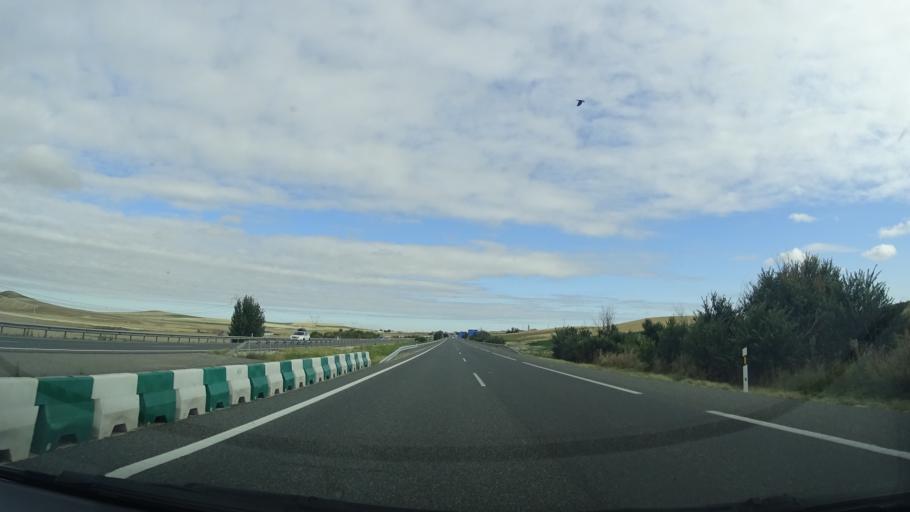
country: ES
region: Castille and Leon
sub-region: Provincia de Valladolid
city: Ataquines
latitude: 41.1630
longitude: -4.7982
